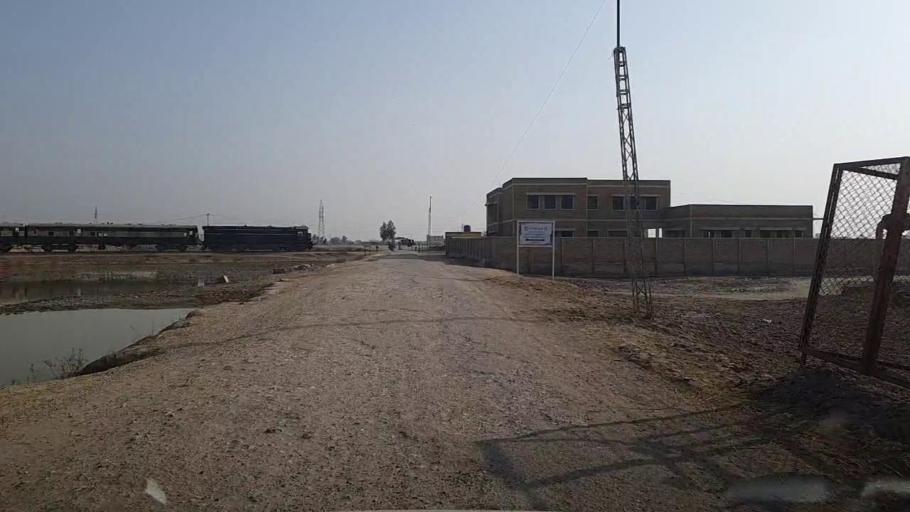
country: PK
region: Sindh
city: Kandhkot
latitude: 28.2770
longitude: 69.2548
